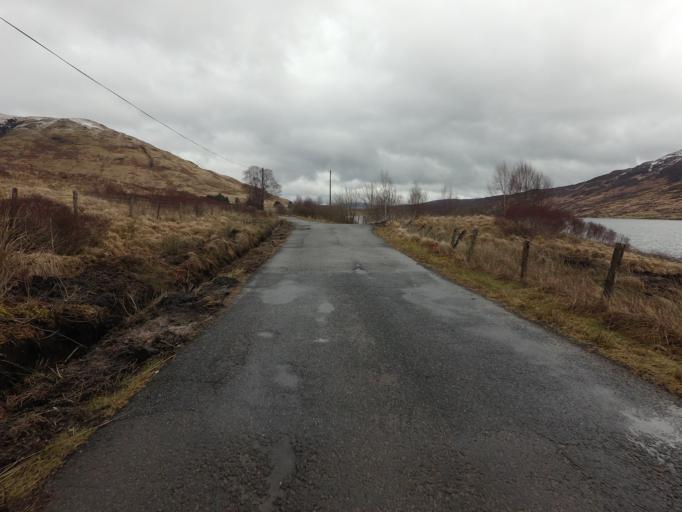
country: GB
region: Scotland
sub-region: West Dunbartonshire
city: Balloch
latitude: 56.2483
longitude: -4.6350
